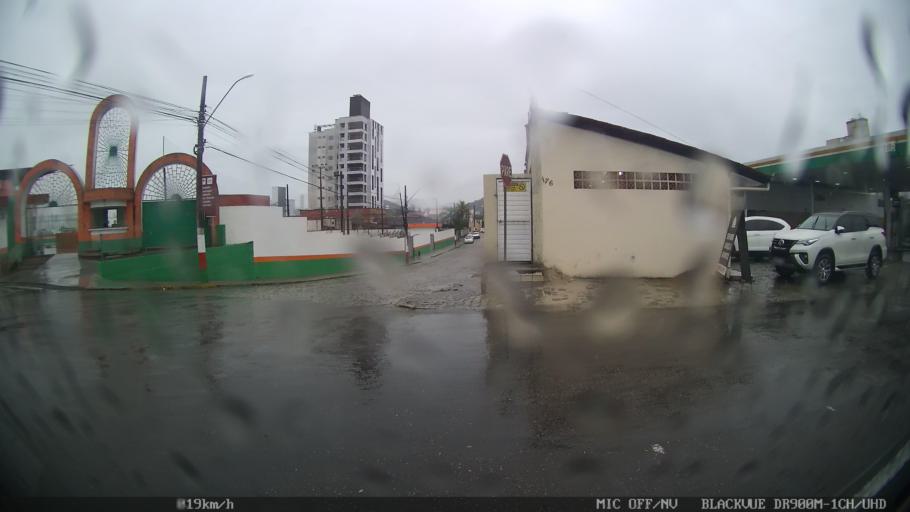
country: BR
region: Santa Catarina
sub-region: Balneario Camboriu
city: Balneario Camboriu
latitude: -27.0222
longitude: -48.6486
